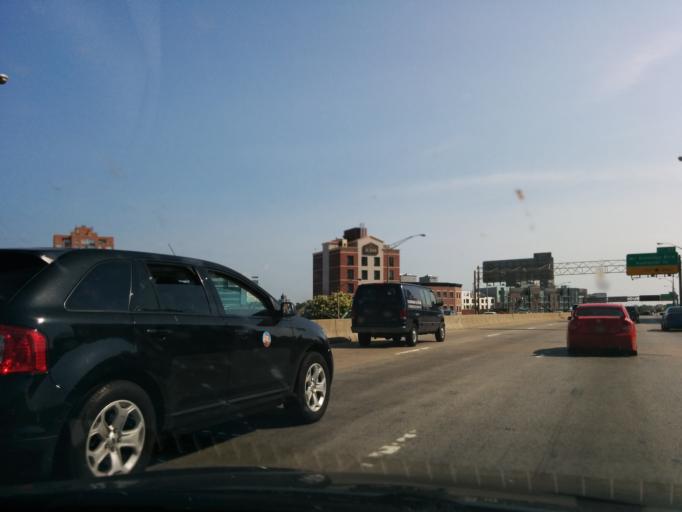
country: US
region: New York
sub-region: Queens County
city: Long Island City
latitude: 40.7154
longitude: -73.9515
